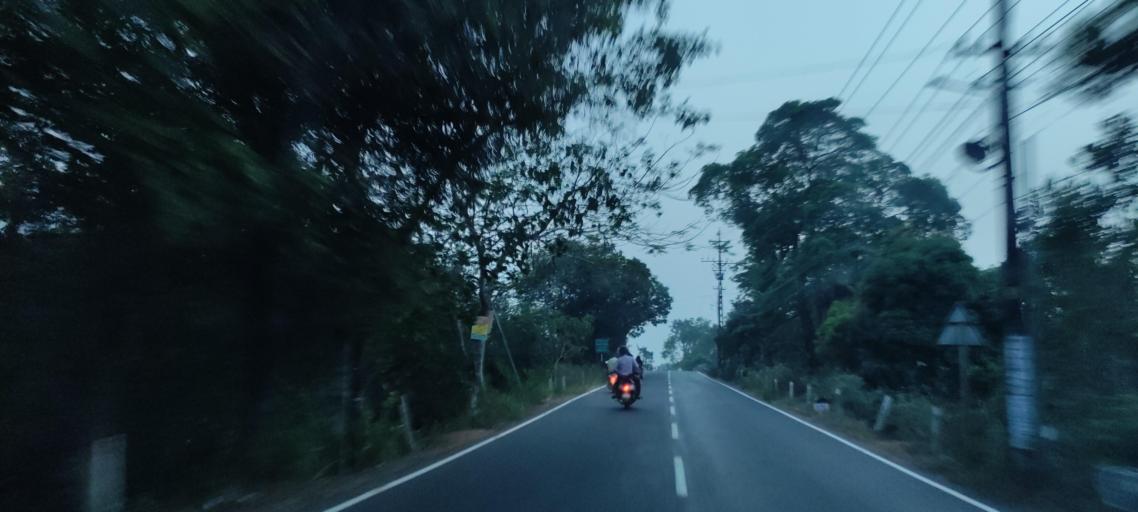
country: IN
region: Kerala
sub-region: Alappuzha
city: Mavelikara
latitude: 9.3271
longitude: 76.4618
